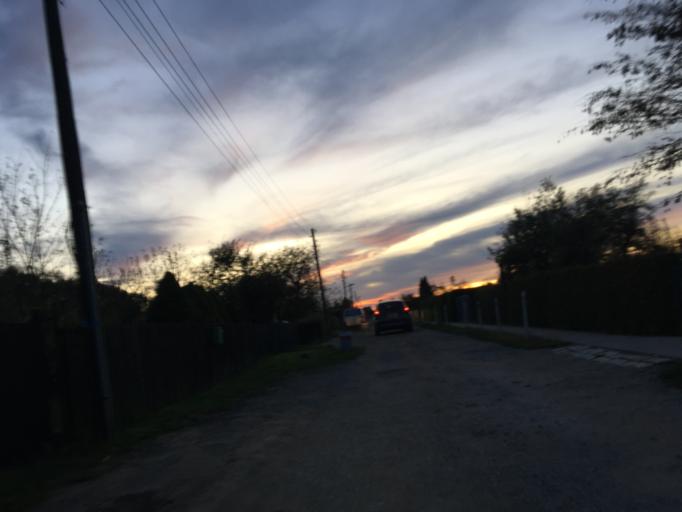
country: DE
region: Berlin
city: Niederschonhausen
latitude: 52.5986
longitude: 13.4088
